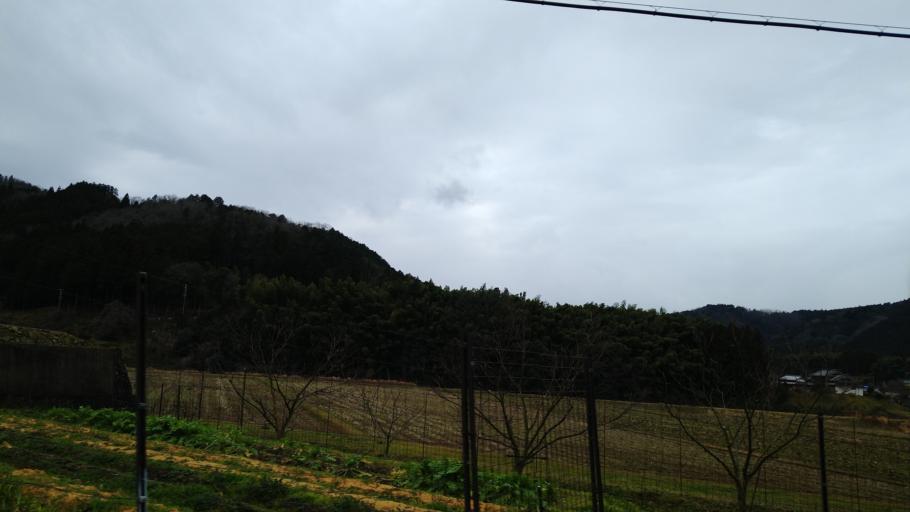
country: JP
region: Kyoto
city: Ayabe
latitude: 35.3323
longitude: 135.3502
